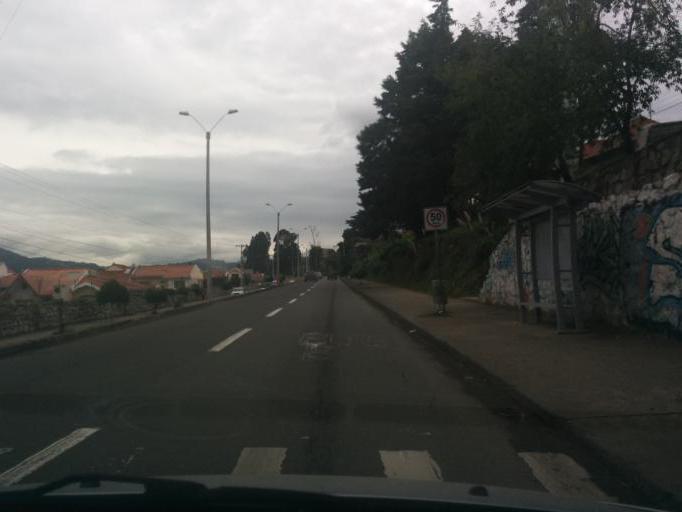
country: EC
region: Azuay
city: Cuenca
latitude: -2.8942
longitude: -78.9710
